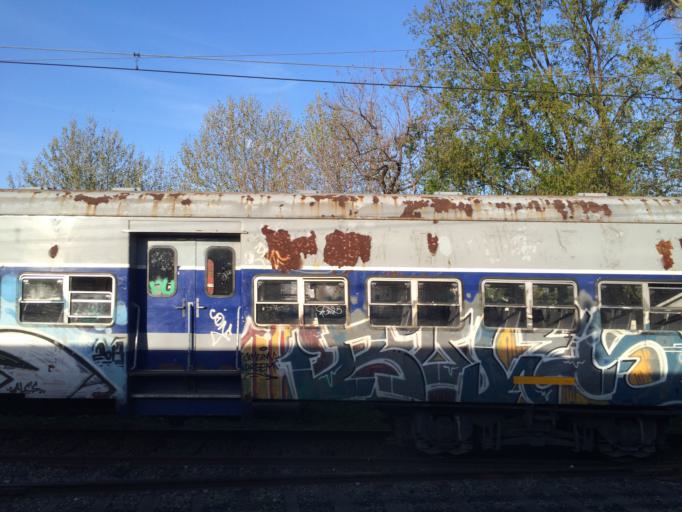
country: AR
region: Buenos Aires
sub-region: Partido de Lomas de Zamora
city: Lomas de Zamora
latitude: -34.7754
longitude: -58.3960
